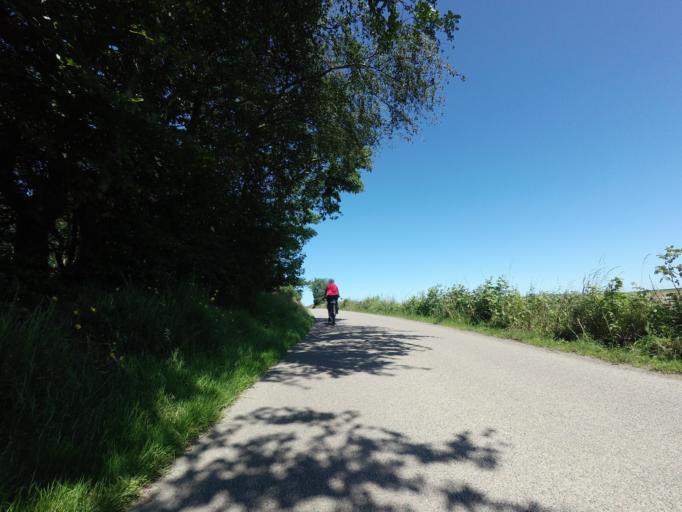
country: GB
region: Scotland
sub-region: Aberdeenshire
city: Macduff
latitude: 57.6456
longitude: -2.5051
